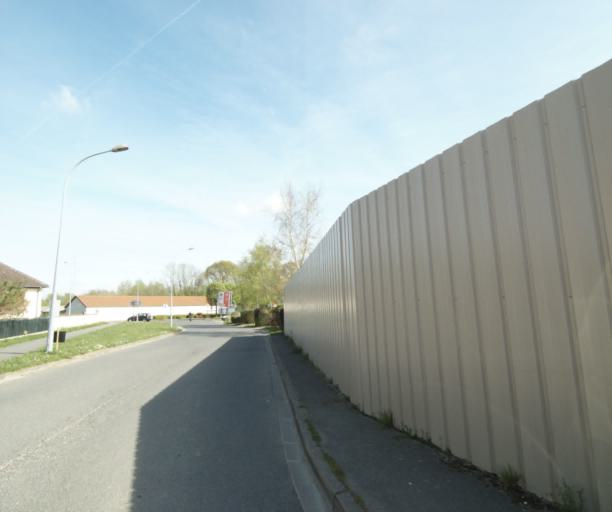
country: FR
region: Ile-de-France
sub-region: Departement de Seine-et-Marne
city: Nangis
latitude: 48.5571
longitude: 3.0243
